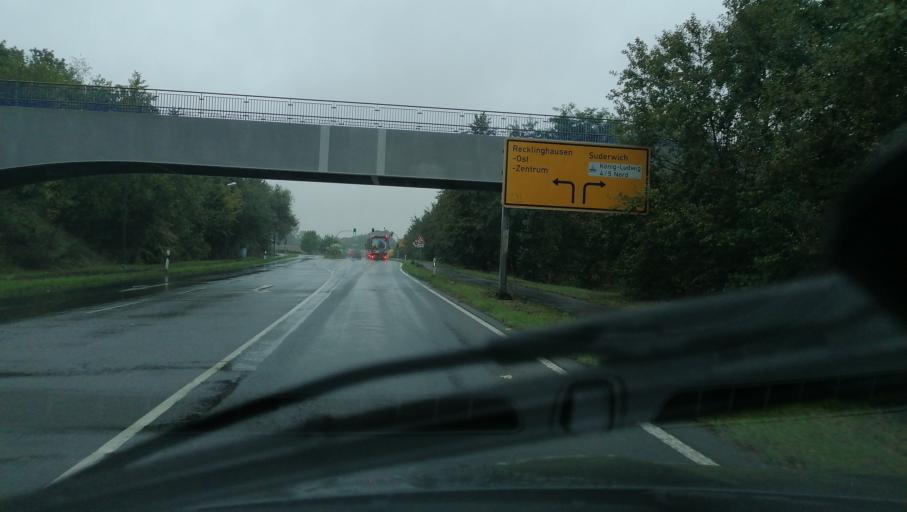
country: DE
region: North Rhine-Westphalia
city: Oer-Erkenschwick
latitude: 51.6041
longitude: 7.2443
